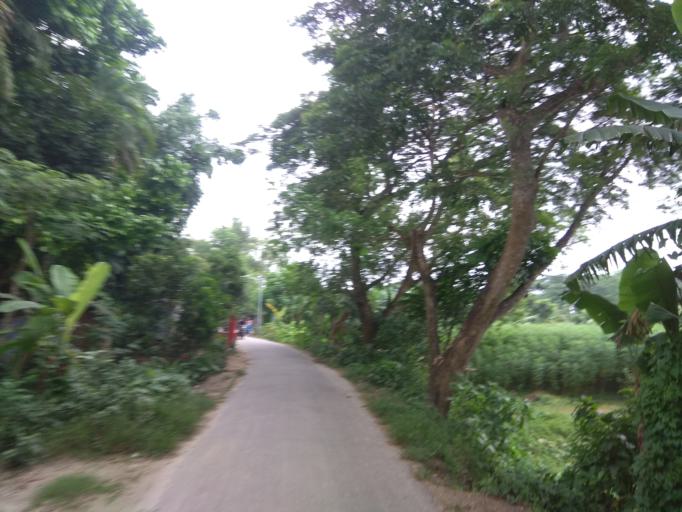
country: BD
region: Dhaka
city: Dohar
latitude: 23.4846
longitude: 90.0009
